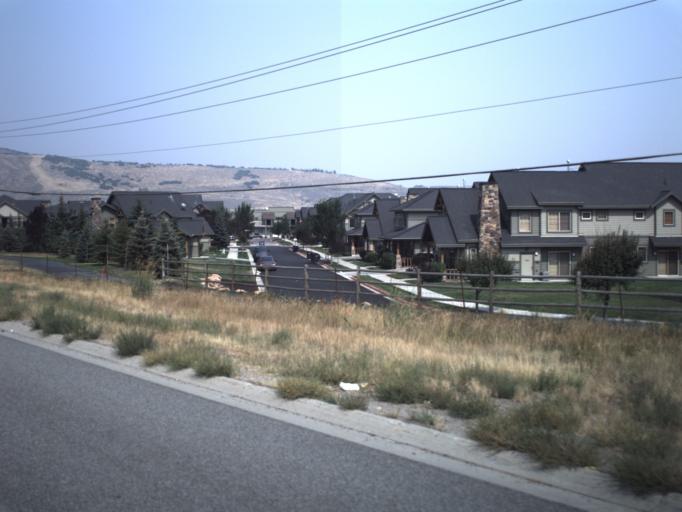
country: US
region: Utah
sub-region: Summit County
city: Snyderville
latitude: 40.7183
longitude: -111.5447
